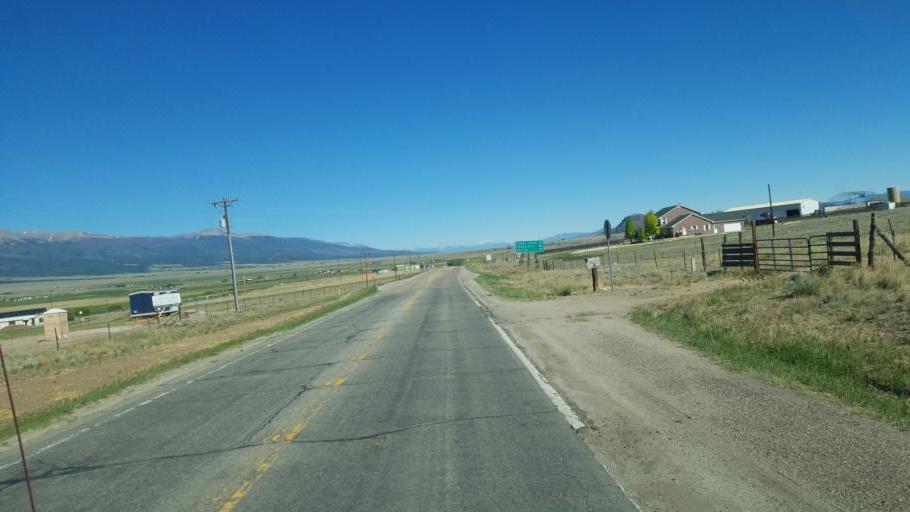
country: US
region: Colorado
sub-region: Custer County
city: Westcliffe
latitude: 38.1399
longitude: -105.4693
